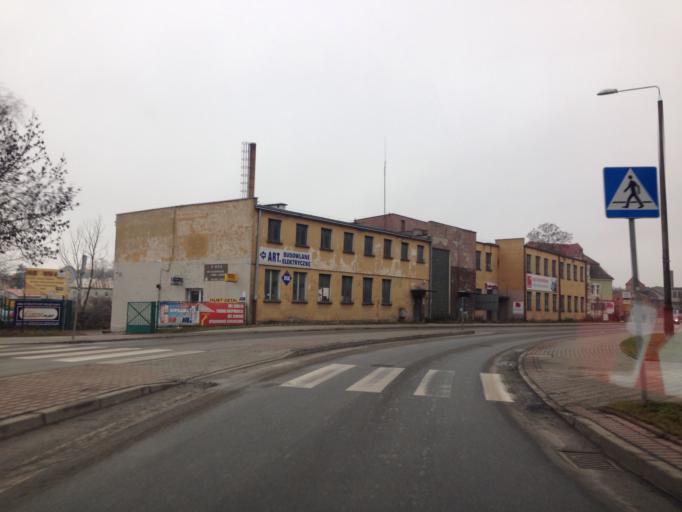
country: PL
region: Warmian-Masurian Voivodeship
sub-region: Powiat ketrzynski
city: Ketrzyn
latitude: 54.0739
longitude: 21.3783
